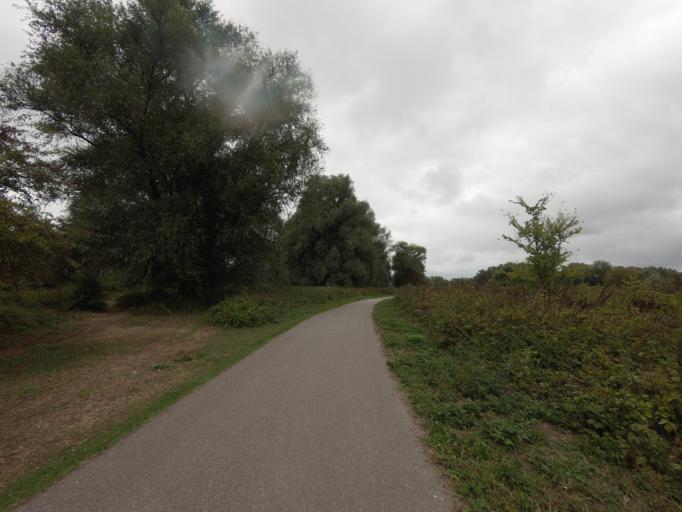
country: NL
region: Gelderland
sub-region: Gemeente Arnhem
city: Sterrenberg
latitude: 51.9711
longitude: 5.8826
